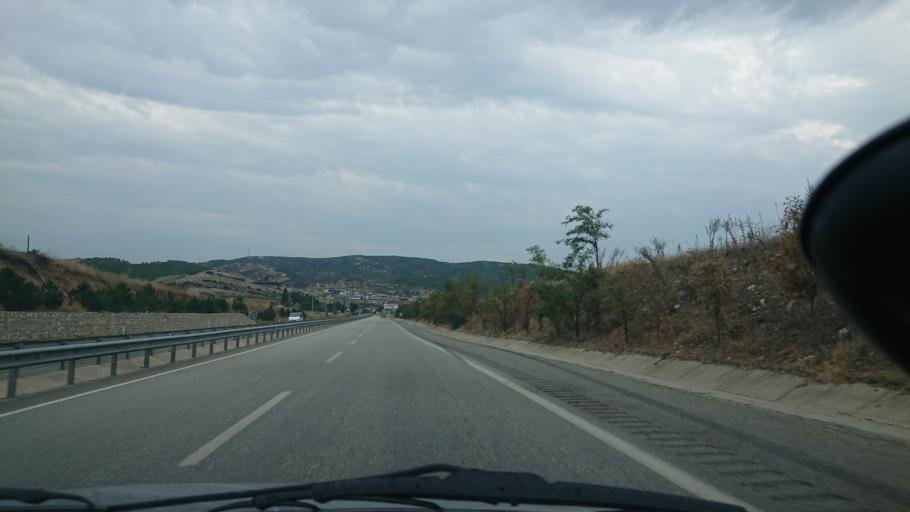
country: TR
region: Manisa
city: Selendi
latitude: 38.5994
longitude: 28.8120
